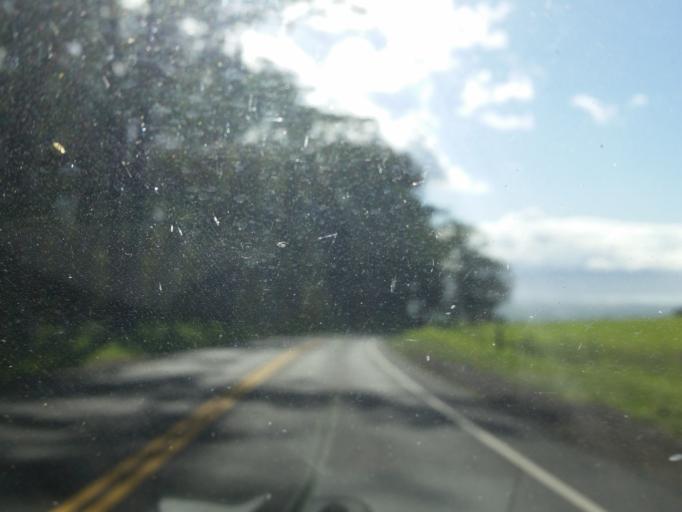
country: US
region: Hawaii
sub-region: Maui County
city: Pukalani
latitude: 20.8212
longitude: -156.3108
